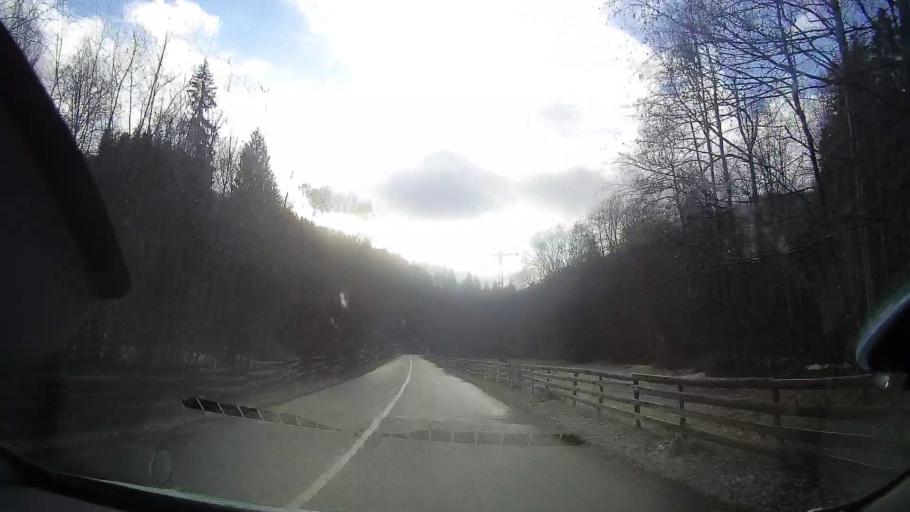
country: RO
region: Alba
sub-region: Comuna Horea
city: Horea
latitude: 46.4819
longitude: 22.9609
